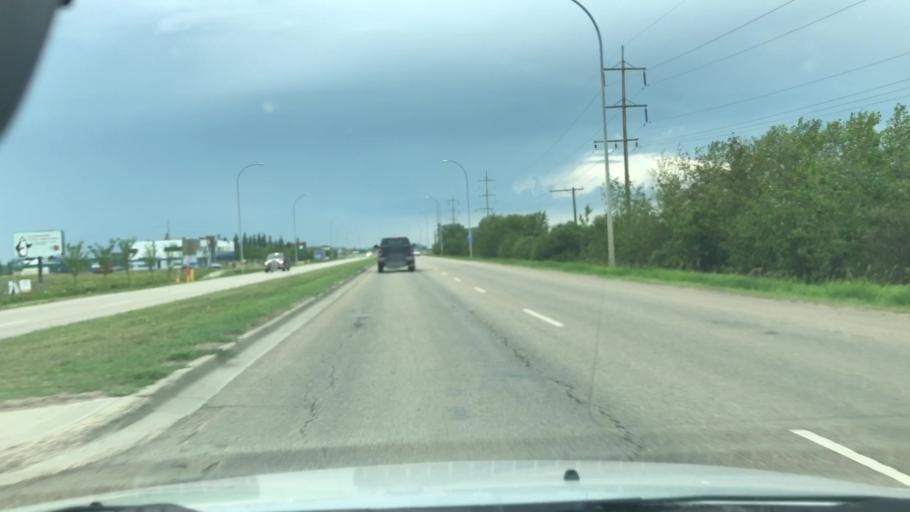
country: CA
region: Alberta
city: St. Albert
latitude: 53.5994
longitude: -113.5971
